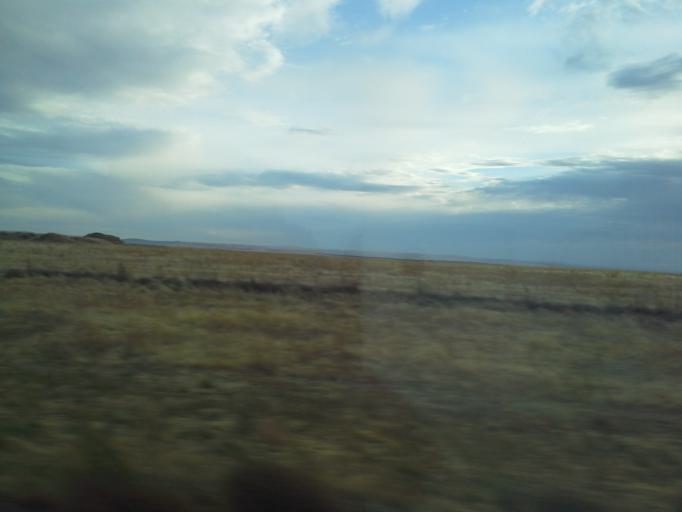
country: US
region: Oregon
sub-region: Umatilla County
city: Stanfield
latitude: 45.7223
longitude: -119.0262
